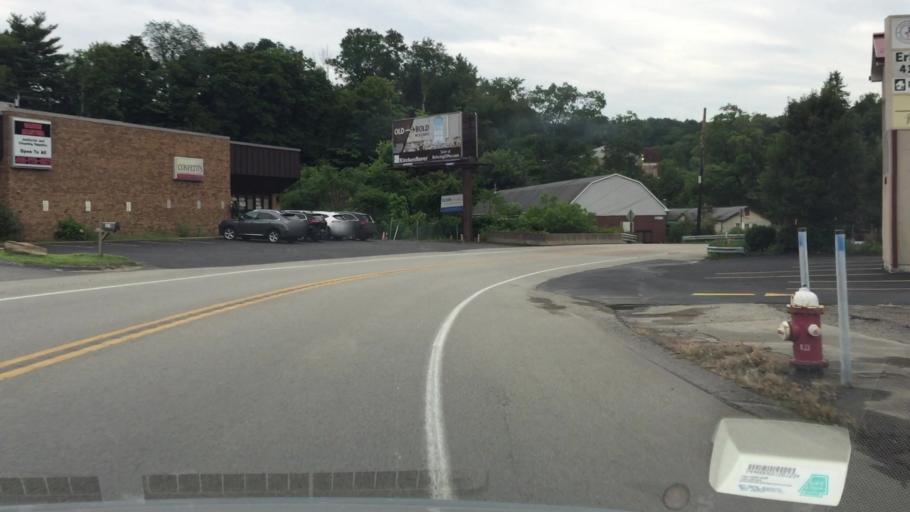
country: US
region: Pennsylvania
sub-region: Allegheny County
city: Millvale
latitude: 40.5074
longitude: -79.9894
